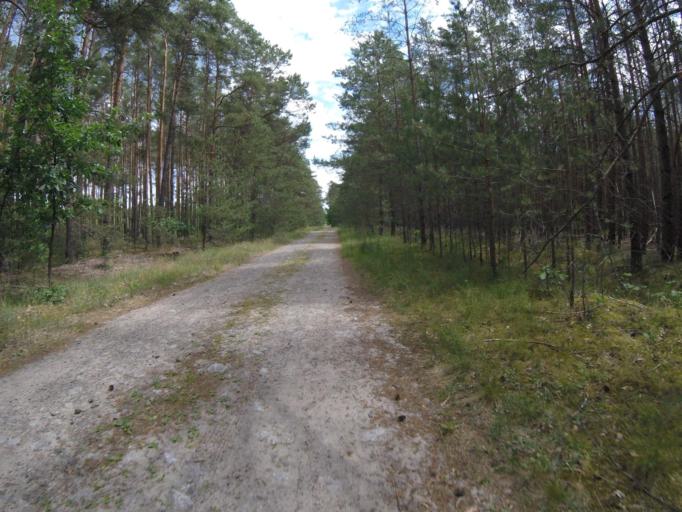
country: DE
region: Brandenburg
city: Halbe
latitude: 52.1049
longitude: 13.6880
